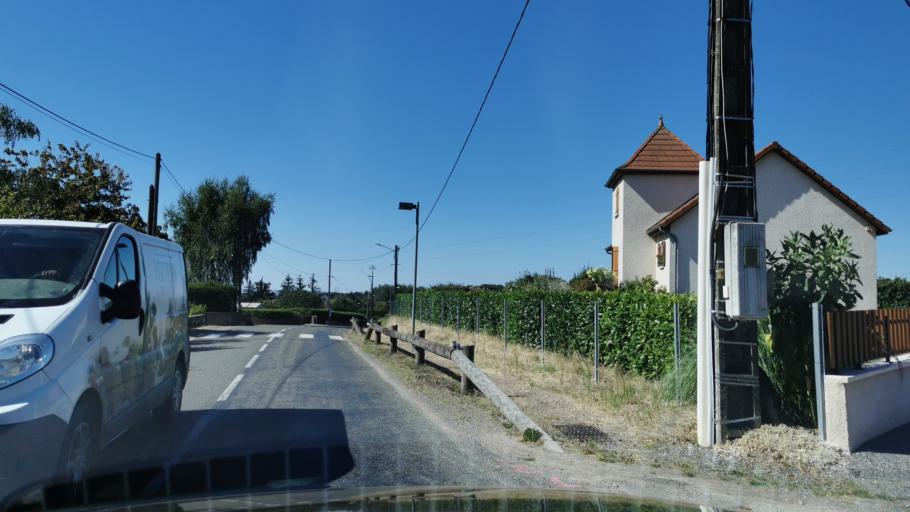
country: FR
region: Bourgogne
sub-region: Departement de Saone-et-Loire
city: Torcy
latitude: 46.7805
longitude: 4.4768
